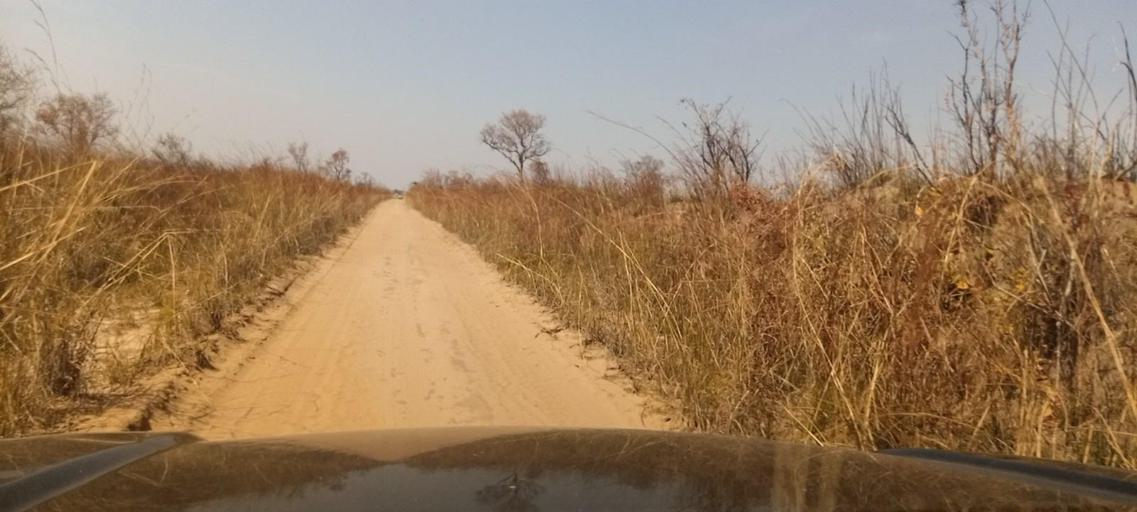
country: CD
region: Kasai-Oriental
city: Kabinda
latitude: -5.7929
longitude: 25.0411
